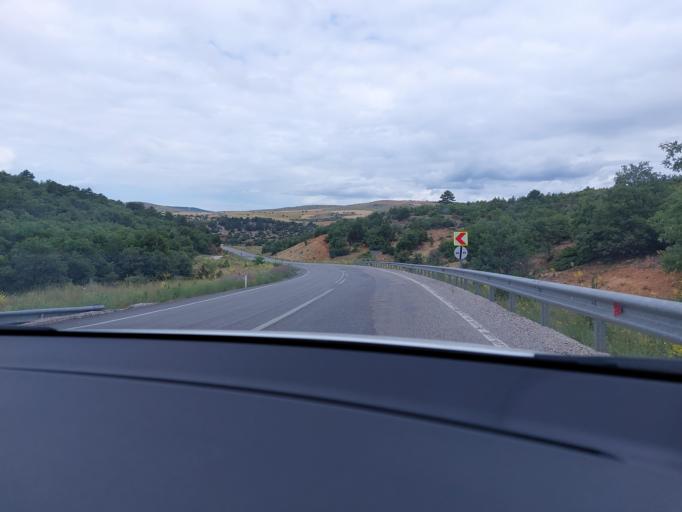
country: TR
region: Konya
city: Doganbey
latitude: 37.8979
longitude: 31.8124
